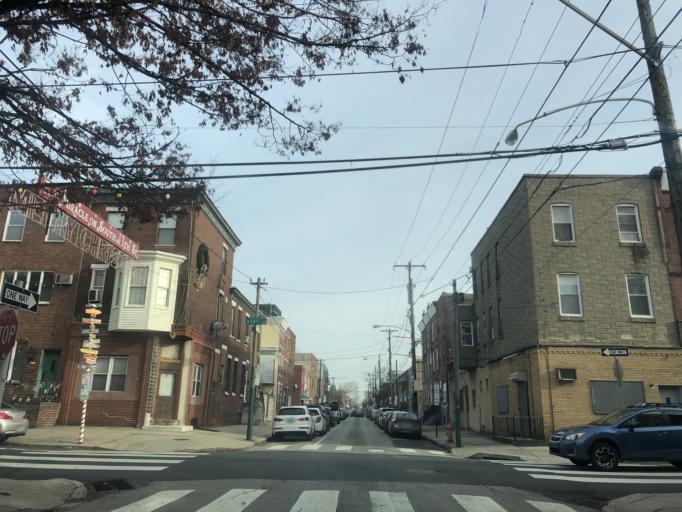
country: US
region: Pennsylvania
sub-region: Philadelphia County
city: Philadelphia
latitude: 39.9290
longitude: -75.1667
